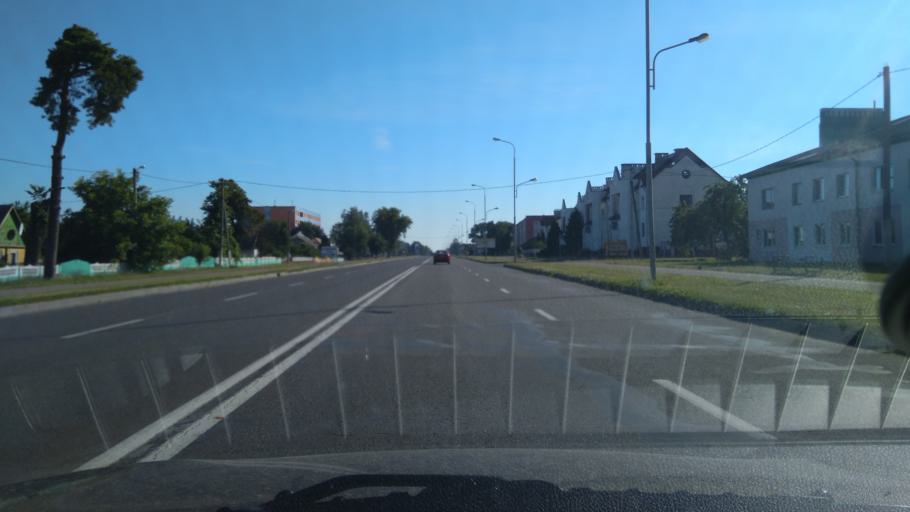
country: BY
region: Brest
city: Ivatsevichy
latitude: 52.7039
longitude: 25.3270
